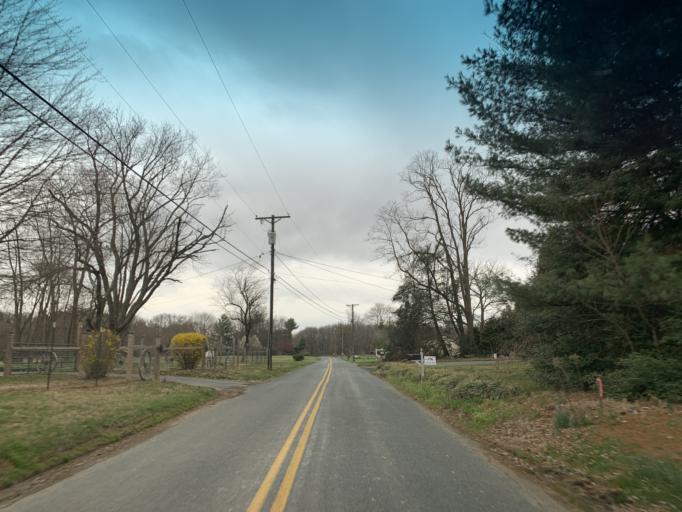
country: US
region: Maryland
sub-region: Harford County
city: Aberdeen
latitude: 39.5720
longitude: -76.1975
